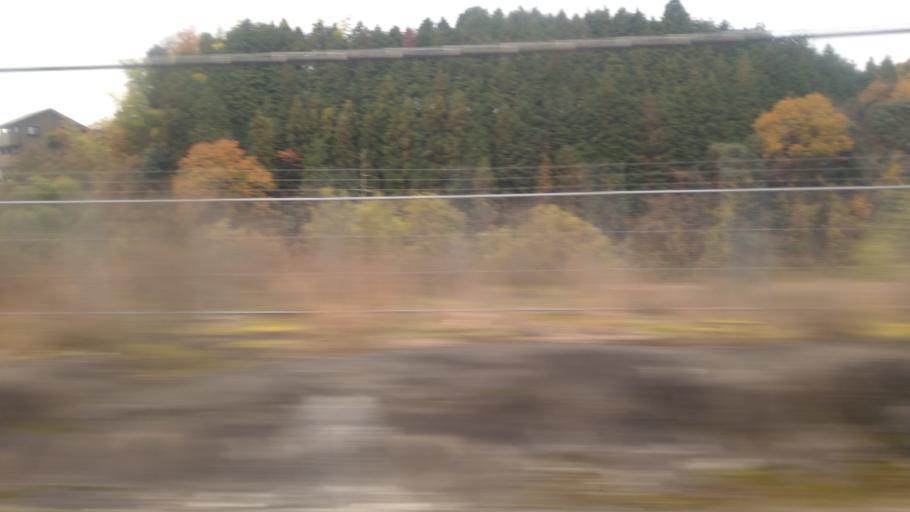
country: JP
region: Gifu
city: Mizunami
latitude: 35.3667
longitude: 137.2231
